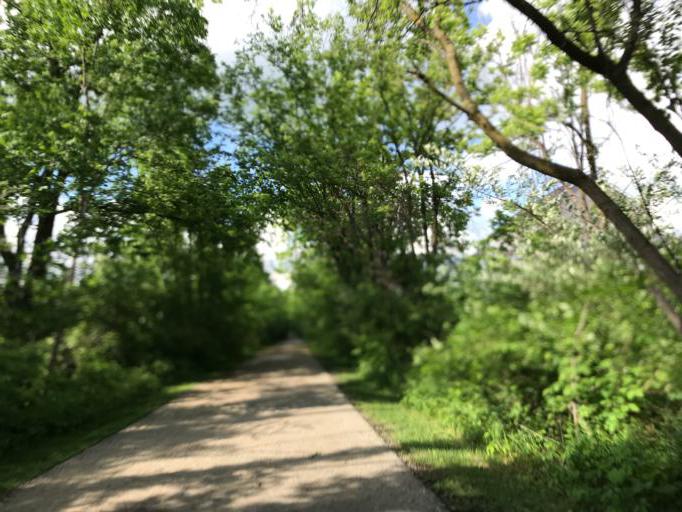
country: US
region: Michigan
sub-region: Oakland County
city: South Lyon
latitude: 42.4704
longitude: -83.6462
